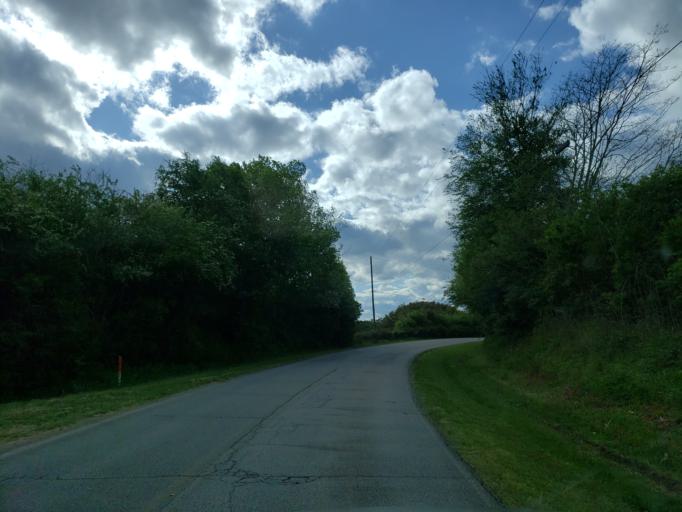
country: US
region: Georgia
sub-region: Haralson County
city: Tallapoosa
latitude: 33.6859
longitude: -85.3007
